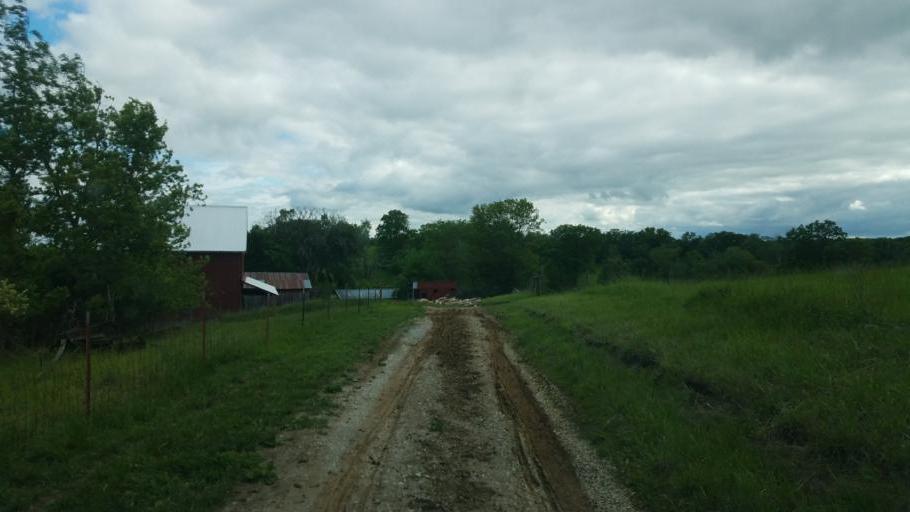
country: US
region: Missouri
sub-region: Mercer County
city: Princeton
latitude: 40.2507
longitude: -93.6861
